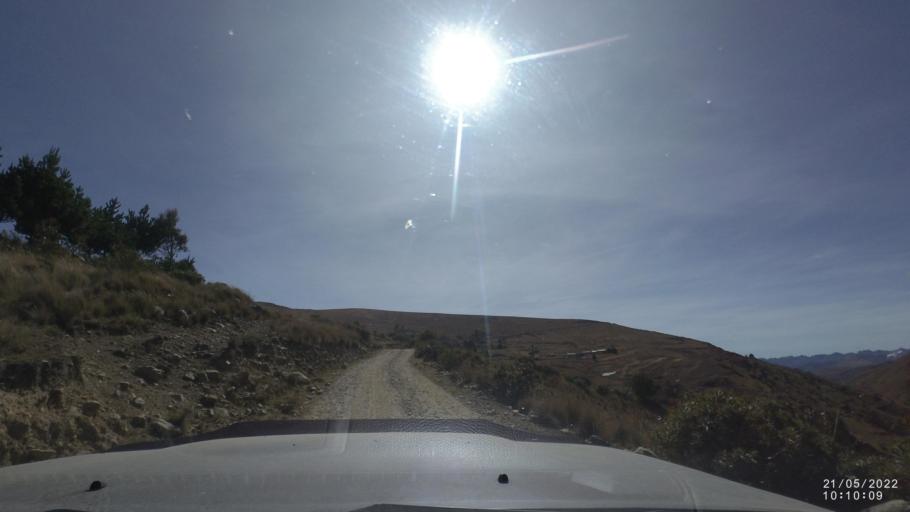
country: BO
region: Cochabamba
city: Colomi
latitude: -17.3366
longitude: -65.9833
